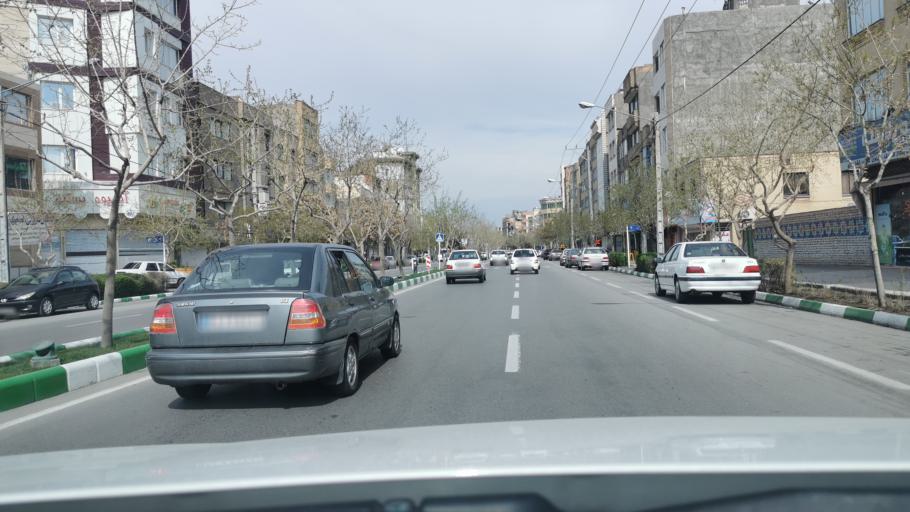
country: IR
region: Razavi Khorasan
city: Mashhad
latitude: 36.3169
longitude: 59.5985
